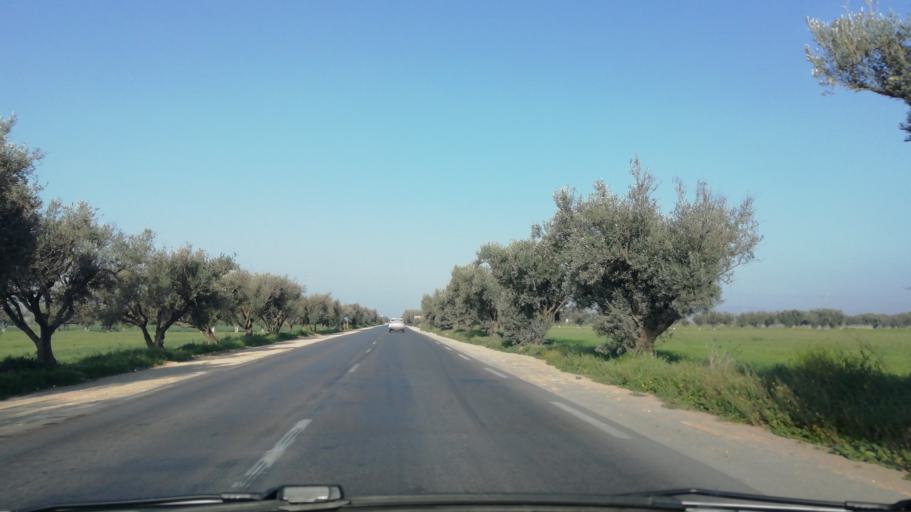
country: DZ
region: Mostaganem
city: Mostaganem
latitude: 35.7479
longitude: 0.1339
